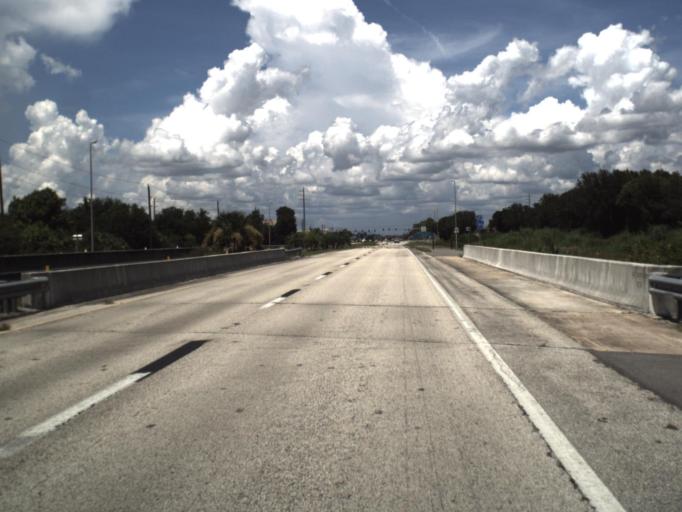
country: US
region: Florida
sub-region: Charlotte County
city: Charlotte Park
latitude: 26.8875
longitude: -82.0198
